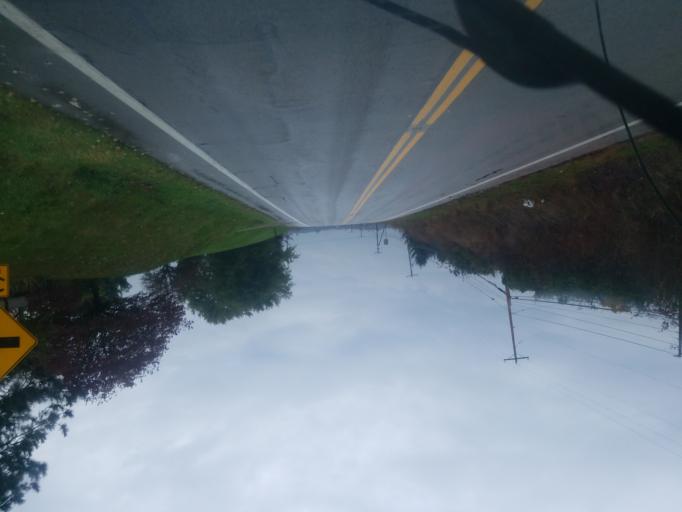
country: US
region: Ohio
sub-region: Muskingum County
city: Frazeysburg
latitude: 40.0321
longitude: -82.1087
